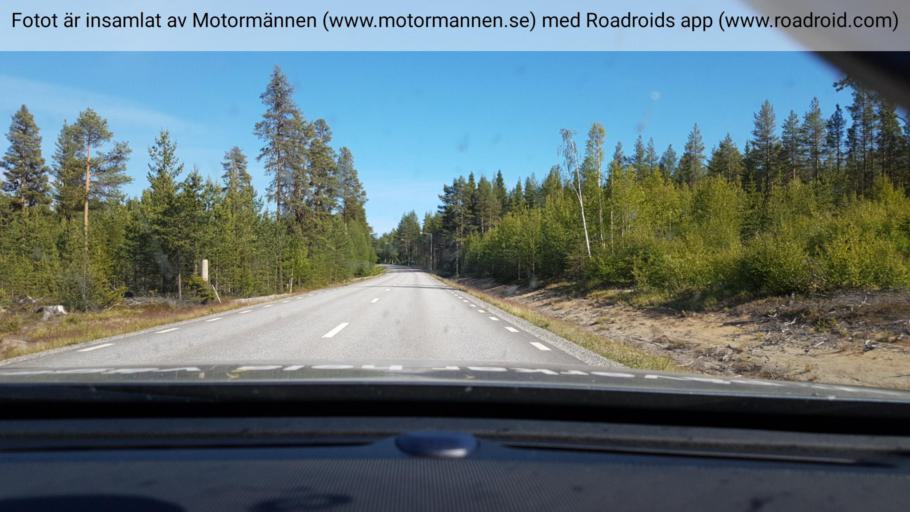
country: SE
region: Vaesterbotten
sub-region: Lycksele Kommun
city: Lycksele
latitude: 64.6417
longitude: 18.5136
